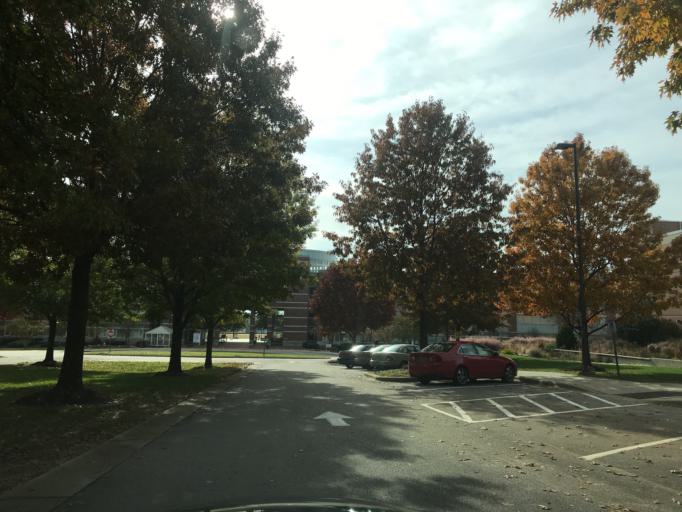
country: US
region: North Carolina
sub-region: Wake County
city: West Raleigh
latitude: 35.7730
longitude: -78.6732
